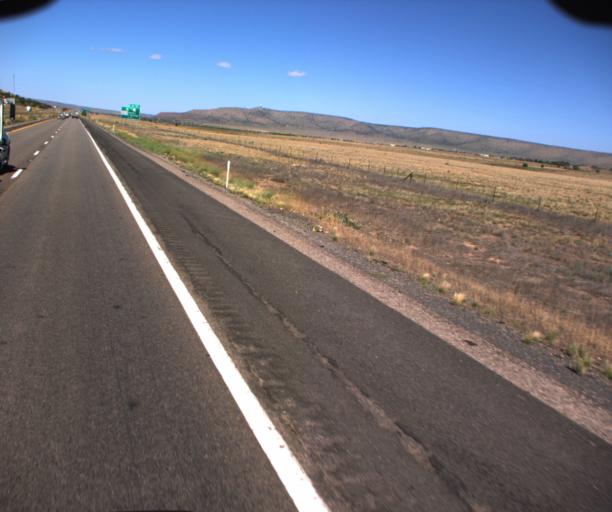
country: US
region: Arizona
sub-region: Yavapai County
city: Paulden
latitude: 35.3161
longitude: -112.8703
